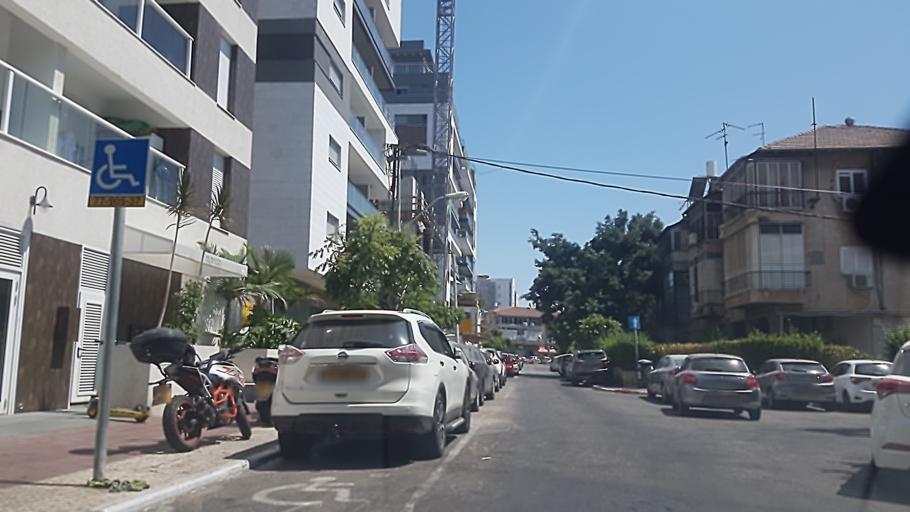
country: IL
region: Tel Aviv
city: Bene Beraq
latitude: 32.0843
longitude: 34.8249
